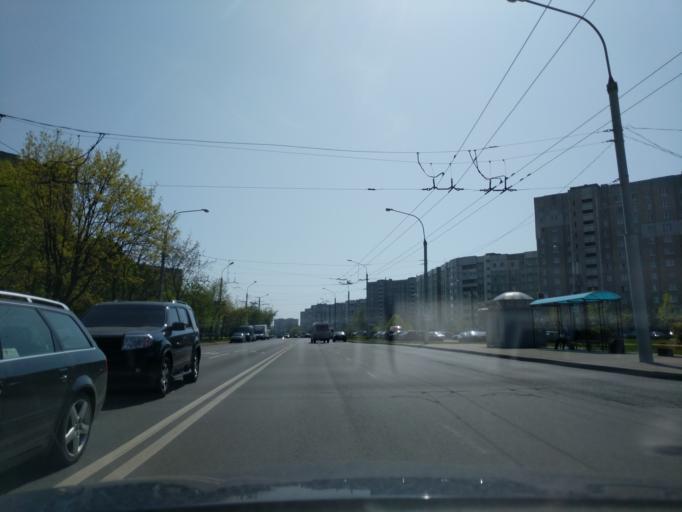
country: BY
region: Minsk
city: Malinovka
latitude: 53.8646
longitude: 27.4539
